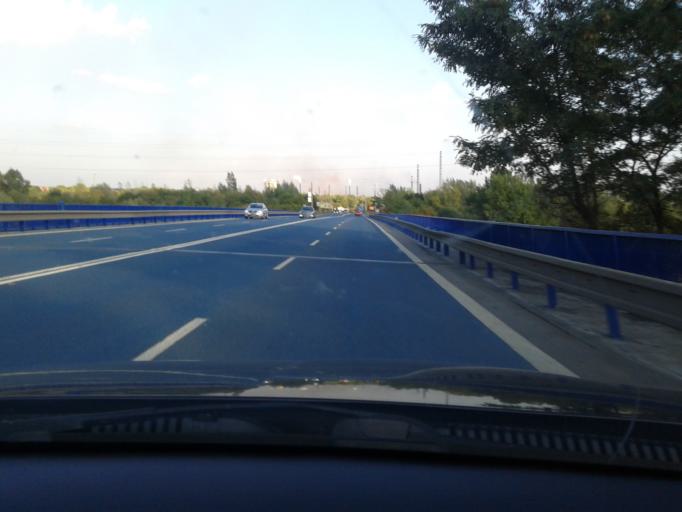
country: CZ
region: Moravskoslezsky
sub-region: Okres Ostrava-Mesto
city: Ostrava
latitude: 49.8056
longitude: 18.2827
